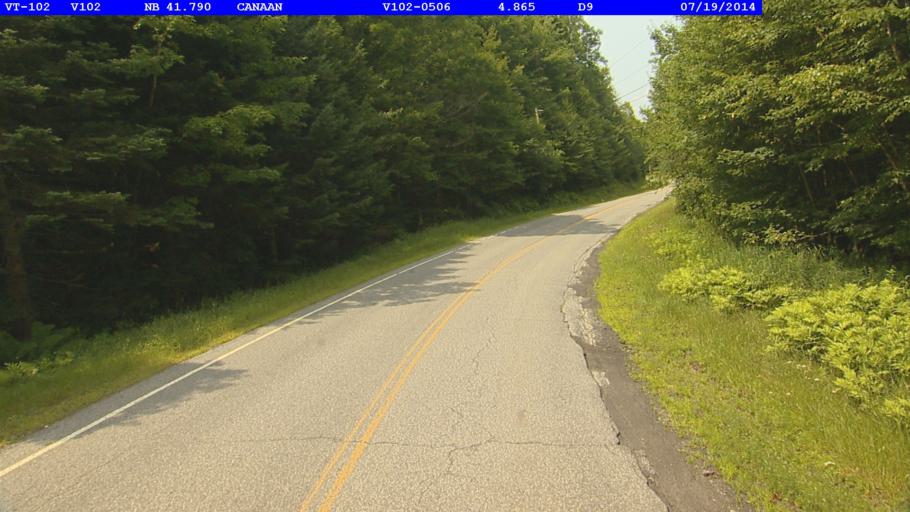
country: US
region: New Hampshire
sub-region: Coos County
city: Colebrook
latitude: 44.9721
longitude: -71.5319
